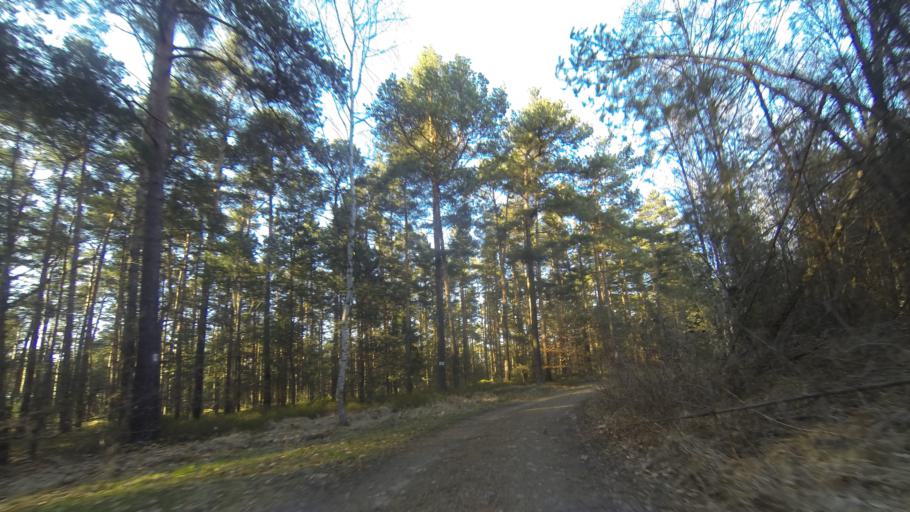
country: DE
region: Saxony
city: Ottendorf-Okrilla
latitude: 51.2098
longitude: 13.8021
